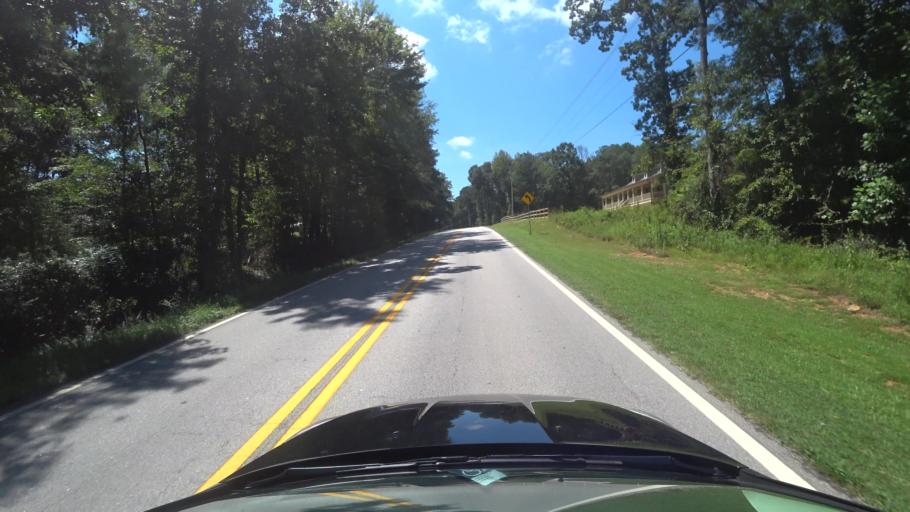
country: US
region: Georgia
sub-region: Newton County
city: Oxford
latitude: 33.6414
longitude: -83.7996
